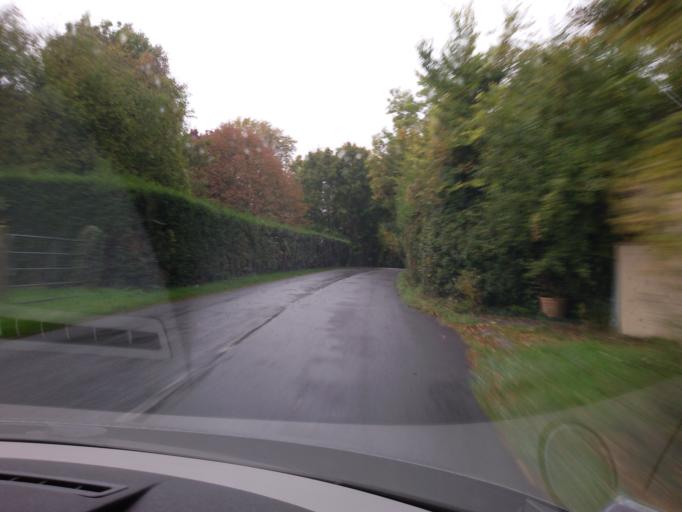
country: FR
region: Lower Normandy
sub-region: Departement du Calvados
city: Trouville-sur-Mer
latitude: 49.4013
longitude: 0.1361
